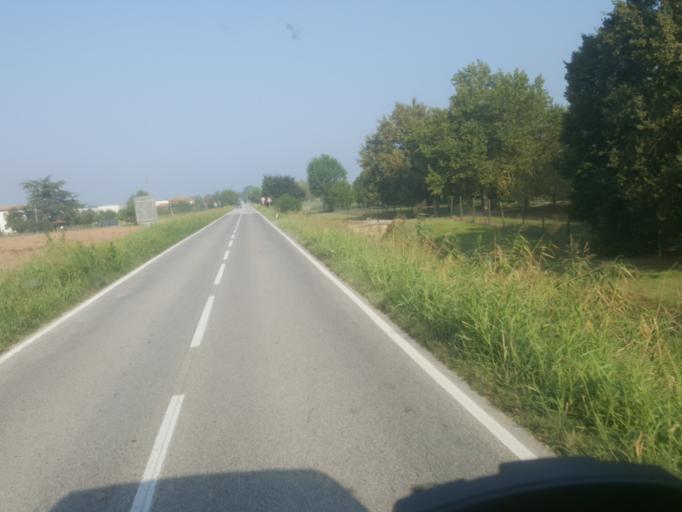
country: IT
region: Emilia-Romagna
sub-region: Provincia di Ravenna
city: Lavezzola
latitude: 44.5680
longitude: 11.8937
